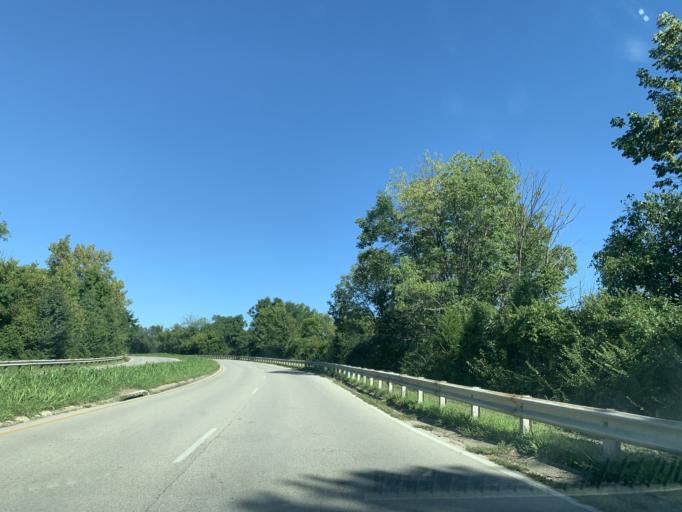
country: US
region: Kentucky
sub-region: Jefferson County
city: West Buechel
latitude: 38.1899
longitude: -85.6696
